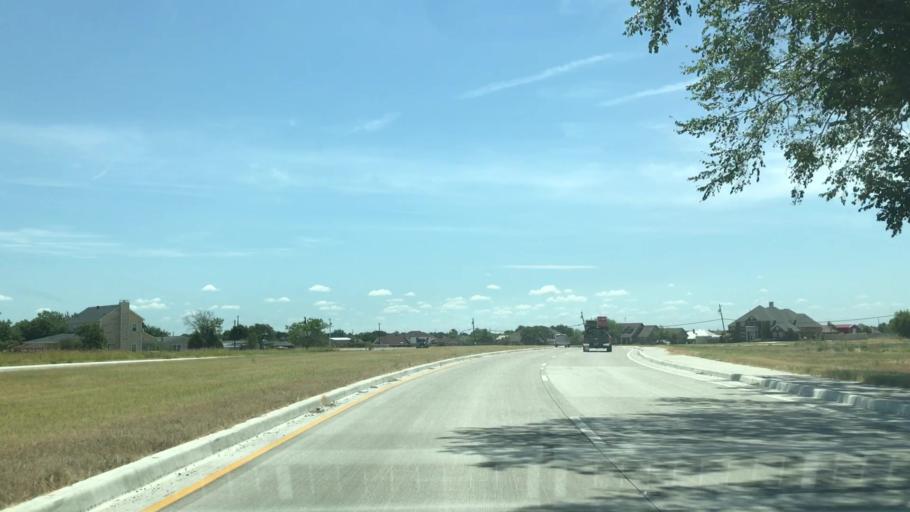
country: US
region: Texas
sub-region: Collin County
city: Saint Paul
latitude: 33.0534
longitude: -96.5652
